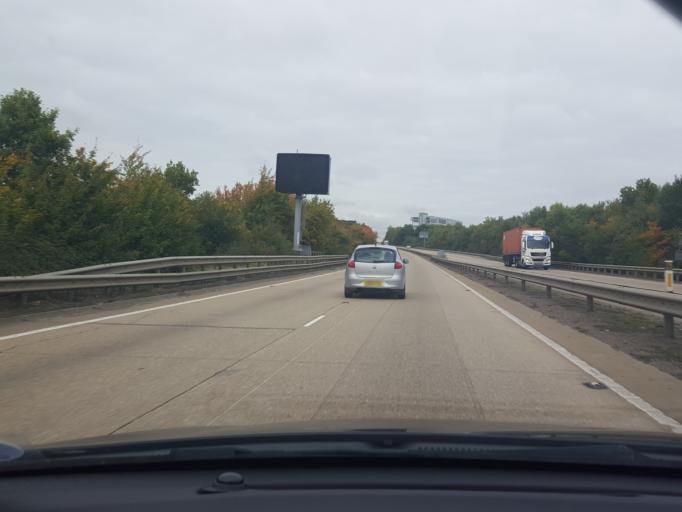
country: GB
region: England
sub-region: Suffolk
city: Bramford
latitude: 52.0748
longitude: 1.1113
